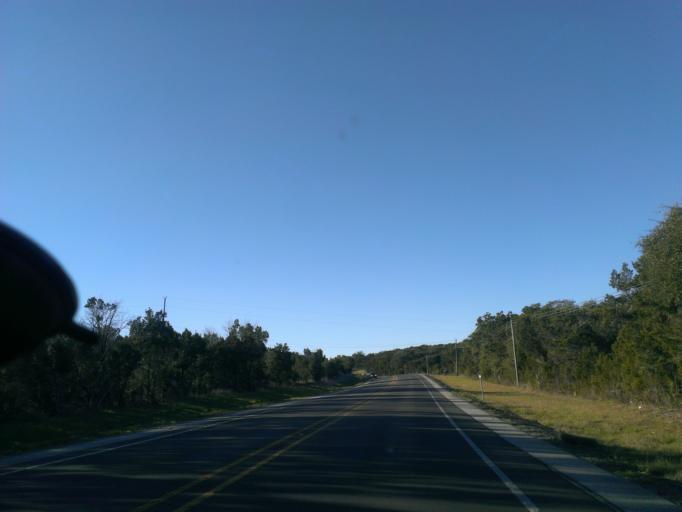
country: US
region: Texas
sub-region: Hays County
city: Dripping Springs
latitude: 30.1345
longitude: -98.0887
